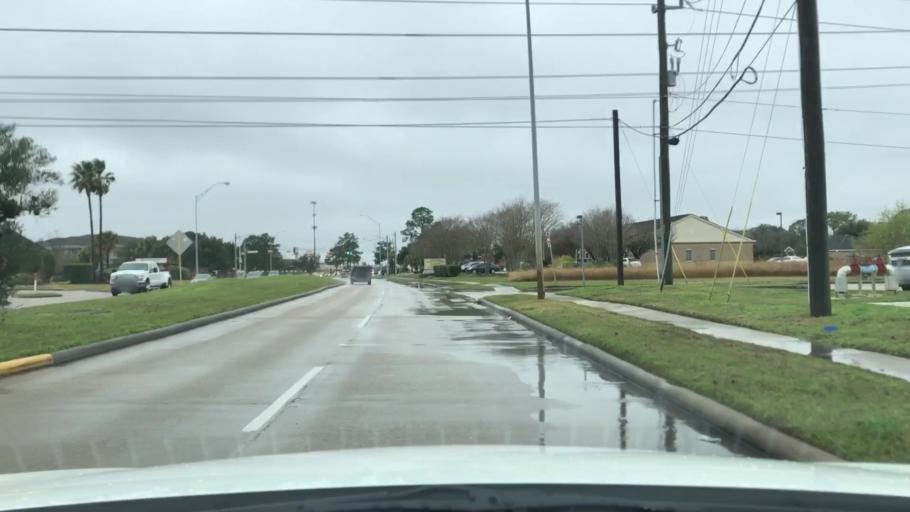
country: US
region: Texas
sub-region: Fort Bend County
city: Cinco Ranch
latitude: 29.7750
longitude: -95.7463
